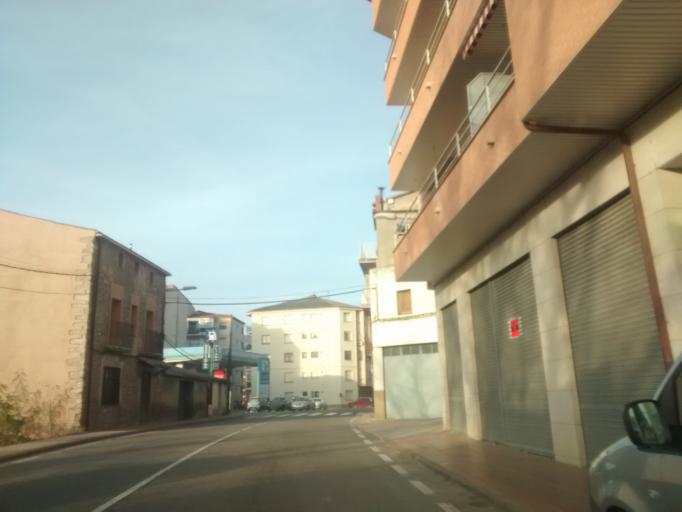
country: ES
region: Catalonia
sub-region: Provincia de Lleida
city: Oliana
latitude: 42.0637
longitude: 1.3129
